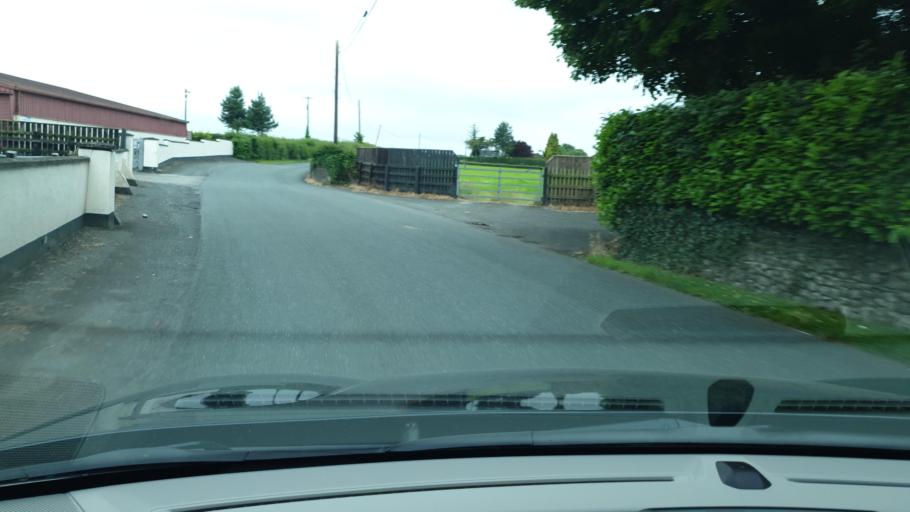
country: IE
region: Leinster
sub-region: An Mhi
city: Dunboyne
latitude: 53.4410
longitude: -6.4827
